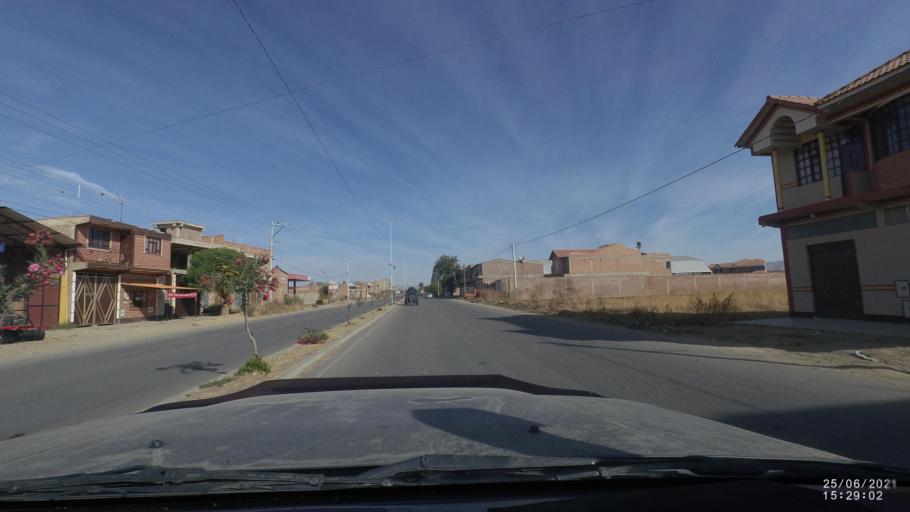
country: BO
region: Cochabamba
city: Cliza
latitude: -17.5671
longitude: -65.9357
